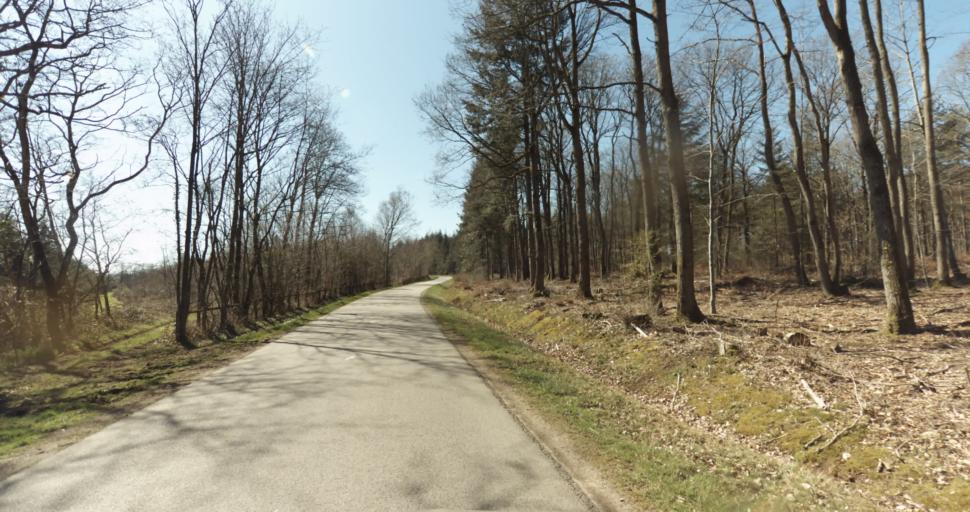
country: FR
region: Lower Normandy
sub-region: Departement du Calvados
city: Livarot
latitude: 48.9703
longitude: 0.1009
